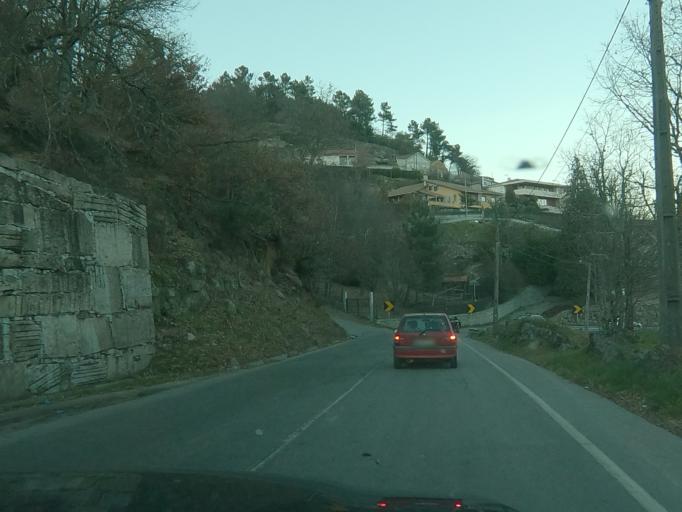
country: PT
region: Vila Real
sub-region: Vila Pouca de Aguiar
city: Vila Pouca de Aguiar
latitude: 41.4981
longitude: -7.6502
